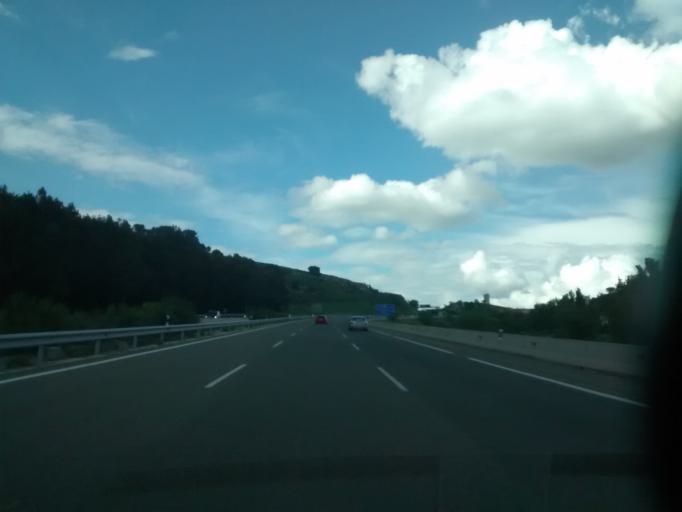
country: ES
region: Castille-La Mancha
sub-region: Provincia de Guadalajara
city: Torija
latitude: 40.7367
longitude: -3.0406
